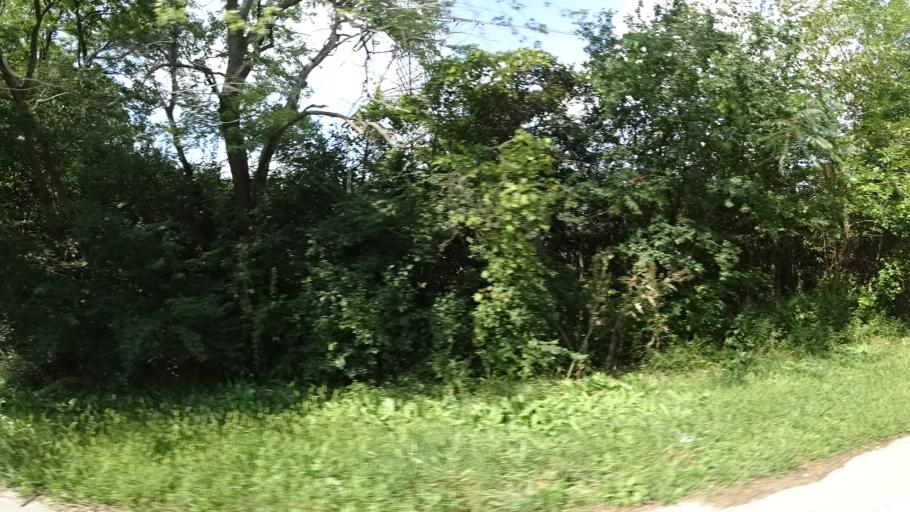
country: US
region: Illinois
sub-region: Will County
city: Goodings Grove
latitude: 41.6512
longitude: -87.9163
